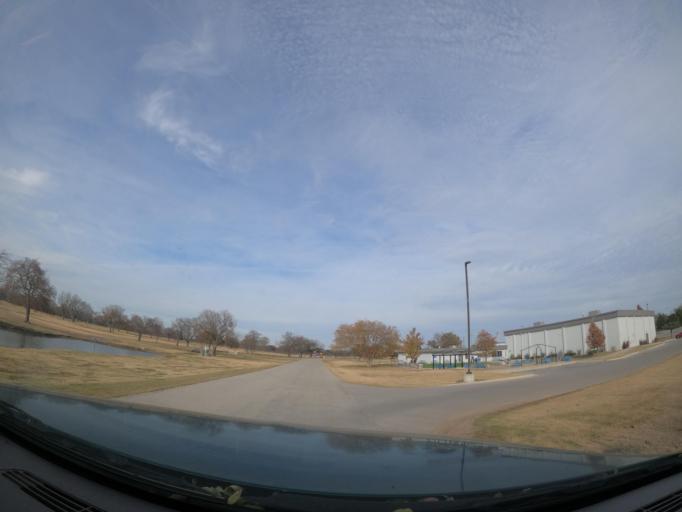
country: US
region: Oklahoma
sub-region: Tulsa County
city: Turley
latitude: 36.2448
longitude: -95.9554
